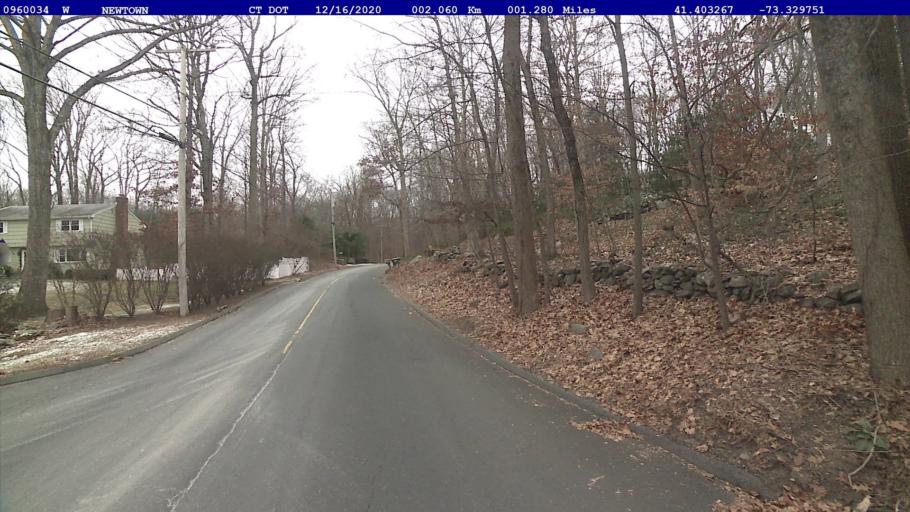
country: US
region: Connecticut
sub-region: Fairfield County
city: Newtown
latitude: 41.4033
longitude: -73.3297
